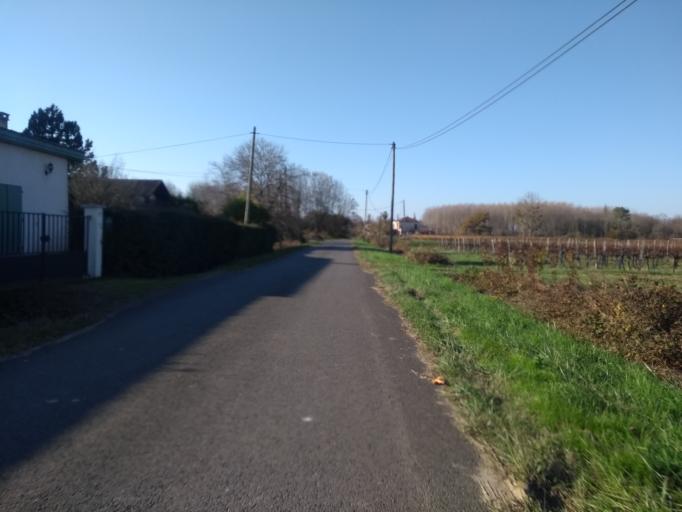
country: FR
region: Aquitaine
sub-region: Departement de la Gironde
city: Cambes
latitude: 44.7301
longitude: -0.4792
